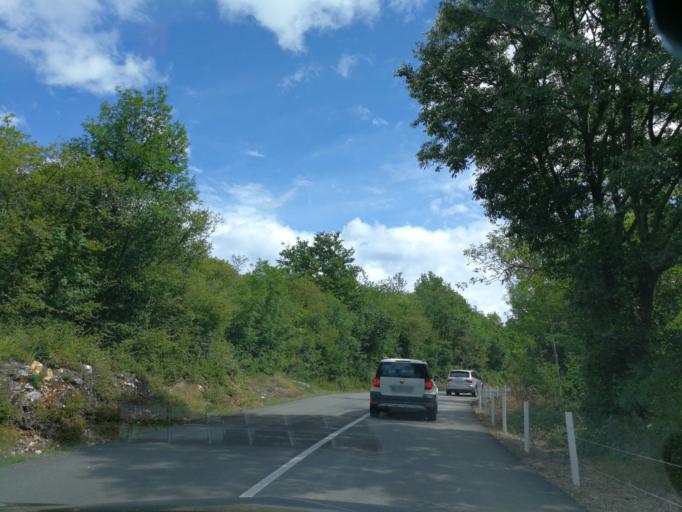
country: HR
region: Primorsko-Goranska
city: Punat
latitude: 45.0807
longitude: 14.6524
